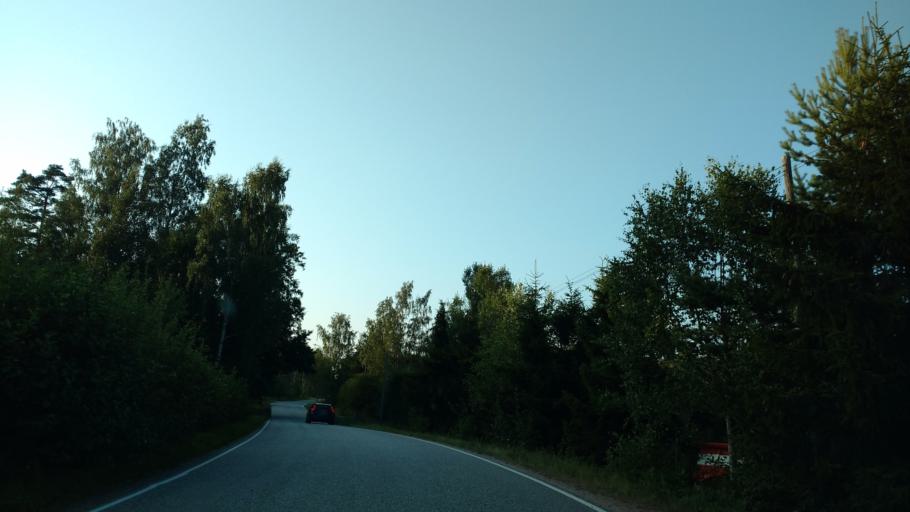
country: FI
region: Varsinais-Suomi
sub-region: Aboland-Turunmaa
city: Dragsfjaerd
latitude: 60.0640
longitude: 22.4518
